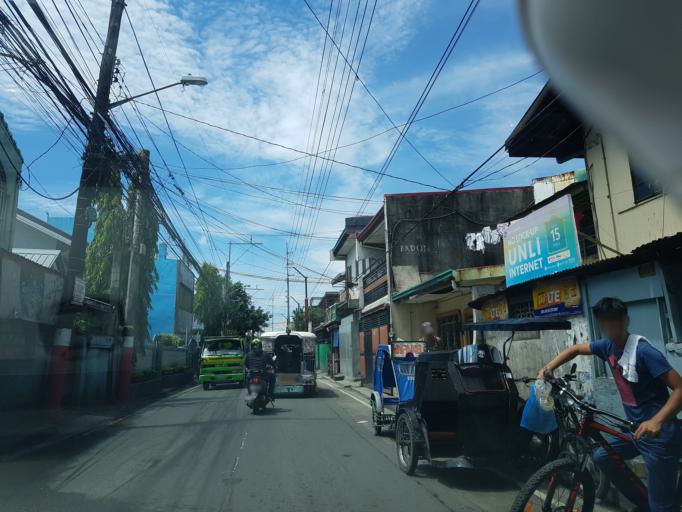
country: PH
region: Calabarzon
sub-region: Province of Rizal
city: Taguig
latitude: 14.5154
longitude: 121.0715
